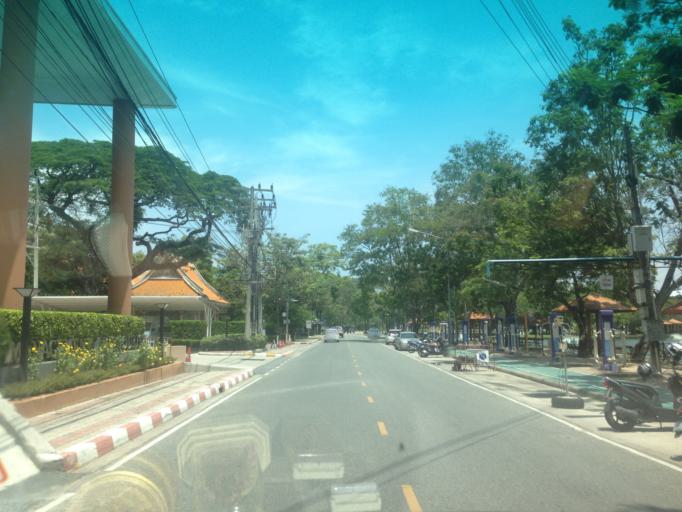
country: TH
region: Chon Buri
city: Si Racha
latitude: 13.2733
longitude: 100.9281
